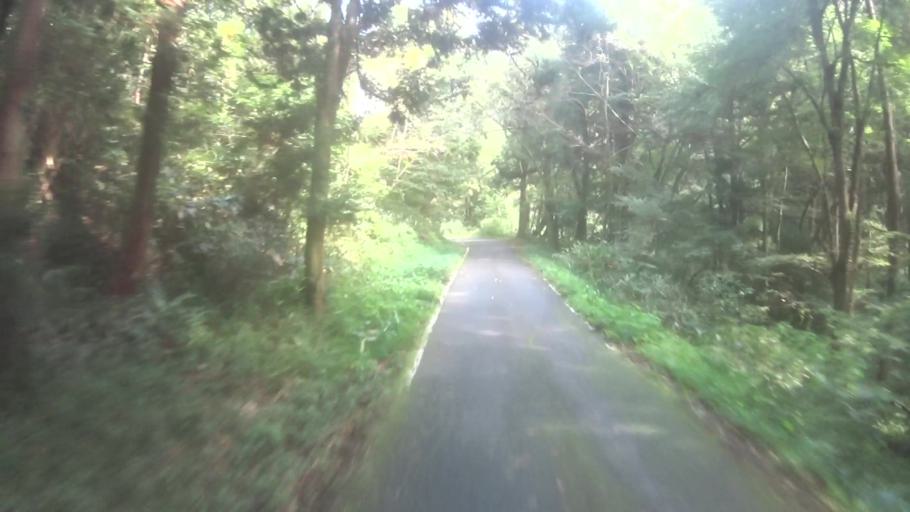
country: JP
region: Kyoto
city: Miyazu
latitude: 35.6092
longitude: 135.1117
